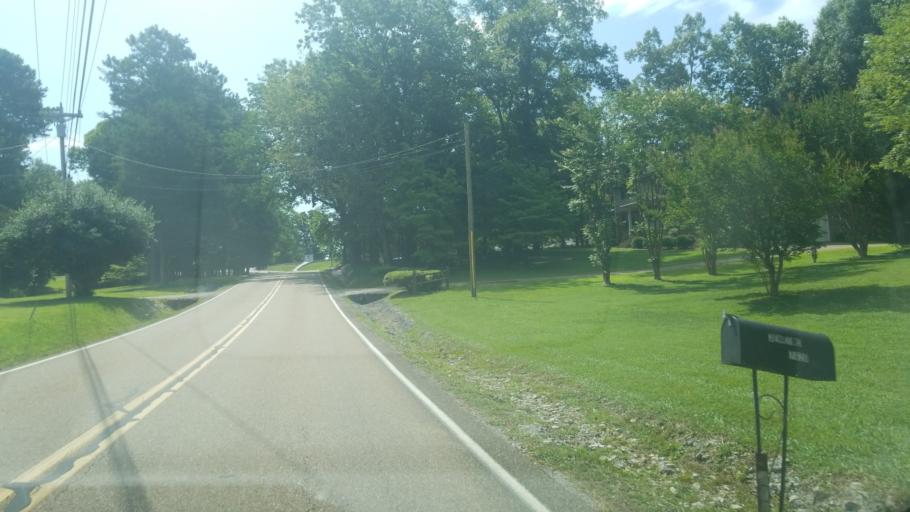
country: US
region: Tennessee
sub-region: Hamilton County
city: Lakesite
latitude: 35.1674
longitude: -85.0603
